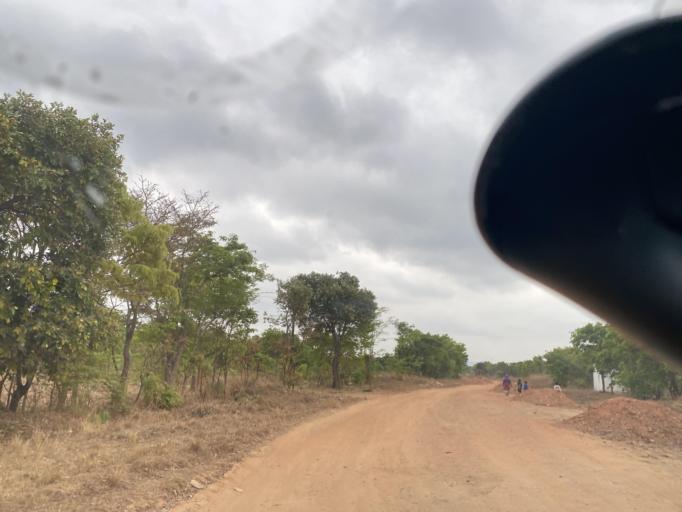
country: ZM
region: Lusaka
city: Chongwe
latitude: -15.2612
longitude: 28.7320
